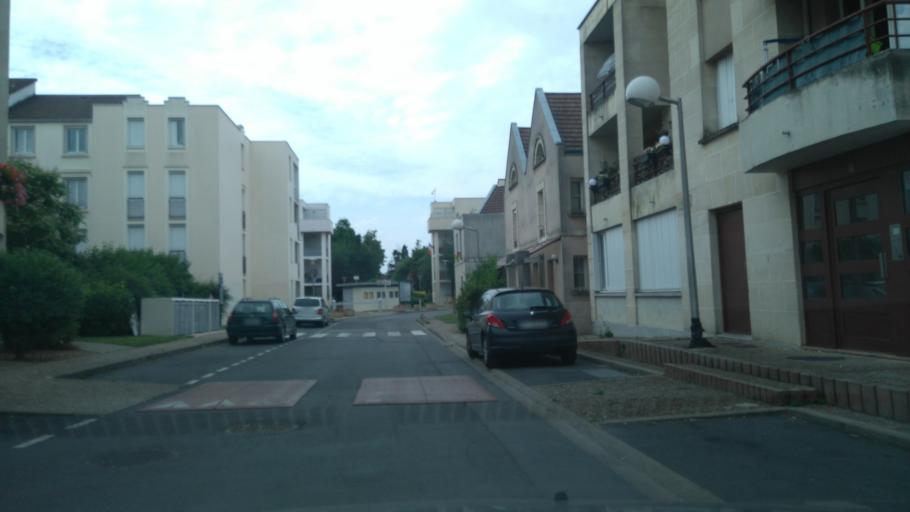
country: FR
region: Picardie
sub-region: Departement de l'Oise
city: Saint-Maximin
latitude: 49.2209
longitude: 2.4434
